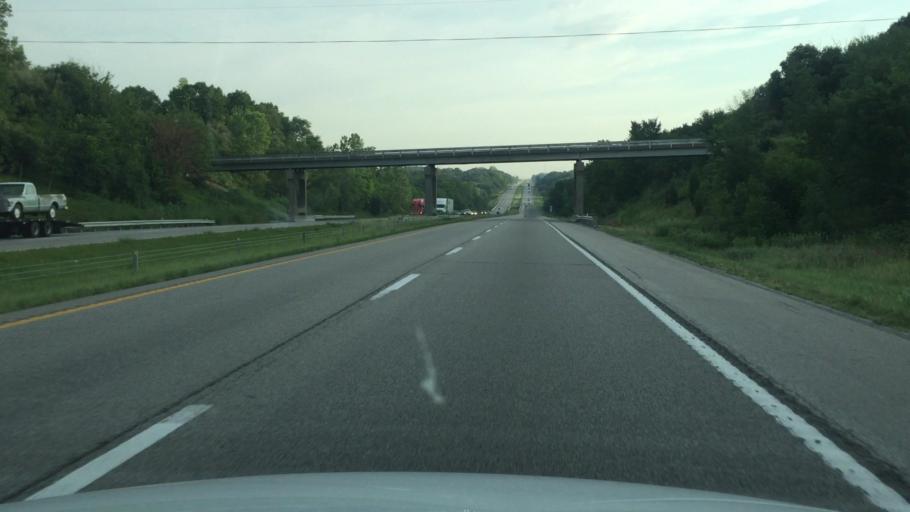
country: US
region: Missouri
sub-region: Buchanan County
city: Saint Joseph
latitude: 39.6511
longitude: -94.7878
